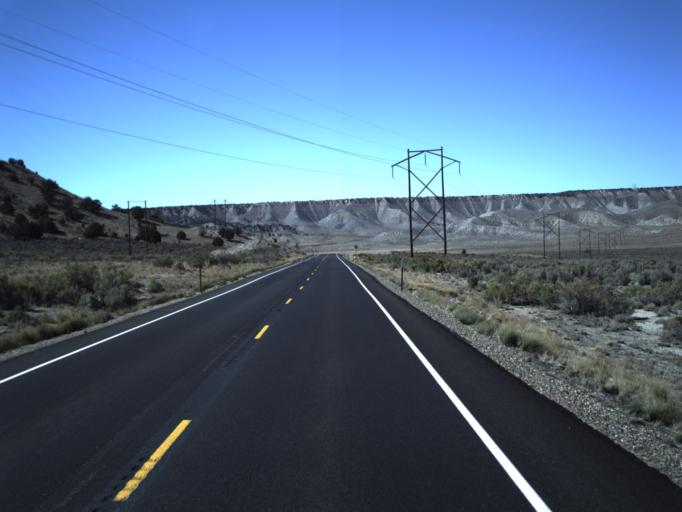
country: US
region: Utah
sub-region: Garfield County
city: Panguitch
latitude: 37.6002
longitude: -111.9557
